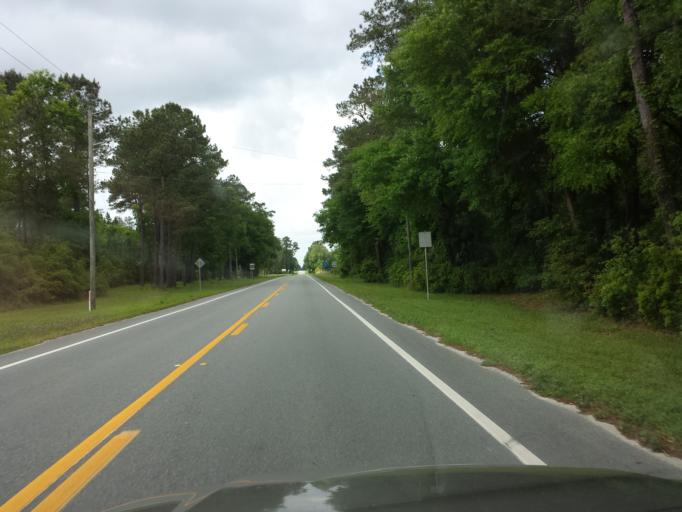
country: US
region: Florida
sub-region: Suwannee County
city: Wellborn
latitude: 30.3418
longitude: -82.7624
